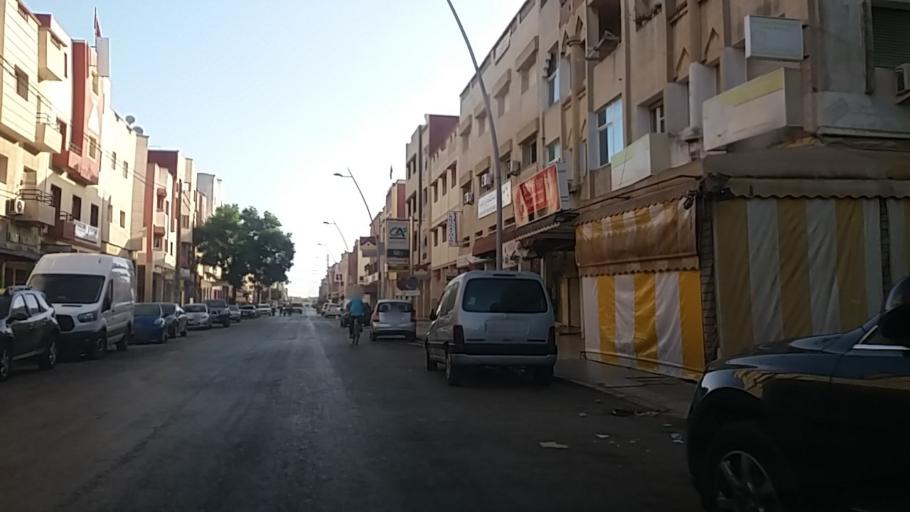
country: MA
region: Gharb-Chrarda-Beni Hssen
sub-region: Kenitra Province
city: Kenitra
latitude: 34.2578
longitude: -6.6217
